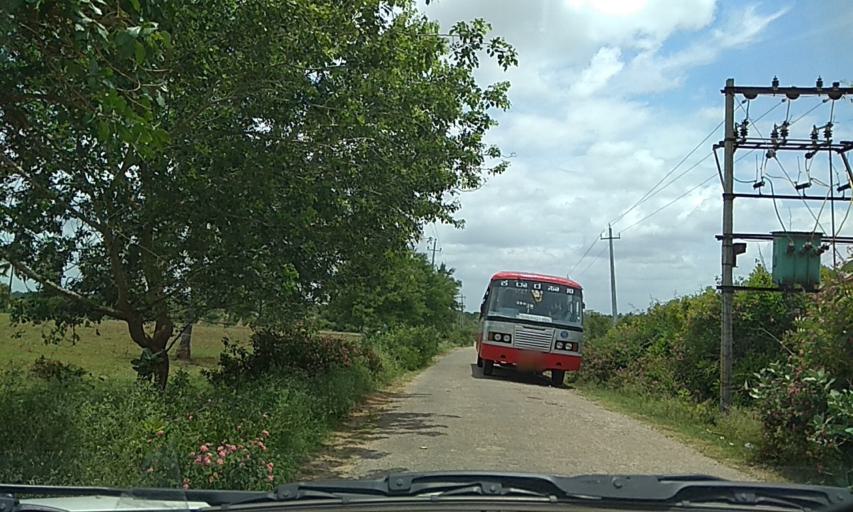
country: IN
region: Karnataka
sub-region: Chamrajnagar
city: Gundlupet
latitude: 11.8868
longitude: 76.6889
